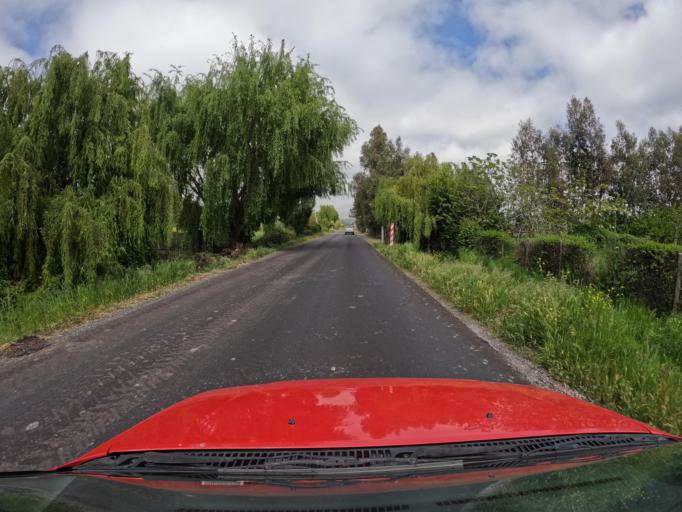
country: CL
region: O'Higgins
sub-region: Provincia de Colchagua
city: Santa Cruz
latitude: -34.6750
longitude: -71.3525
